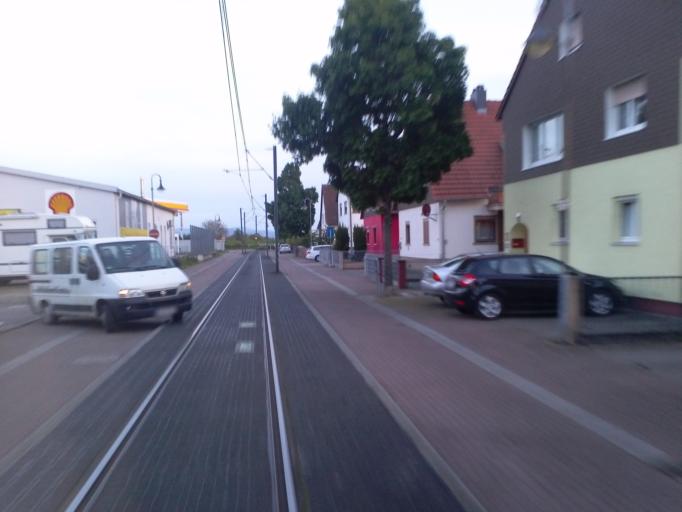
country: DE
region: Baden-Wuerttemberg
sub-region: Karlsruhe Region
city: Rheinstetten
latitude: 48.9557
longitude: 8.2933
